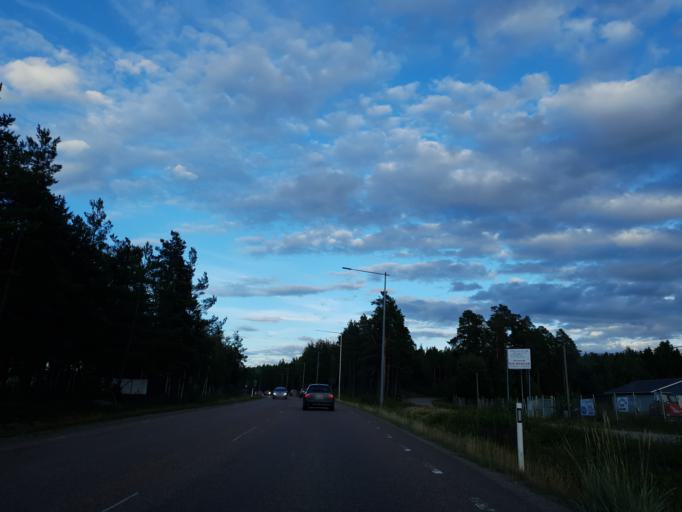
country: SE
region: Gaevleborg
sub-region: Soderhamns Kommun
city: Soderhamn
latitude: 61.2921
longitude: 17.0435
